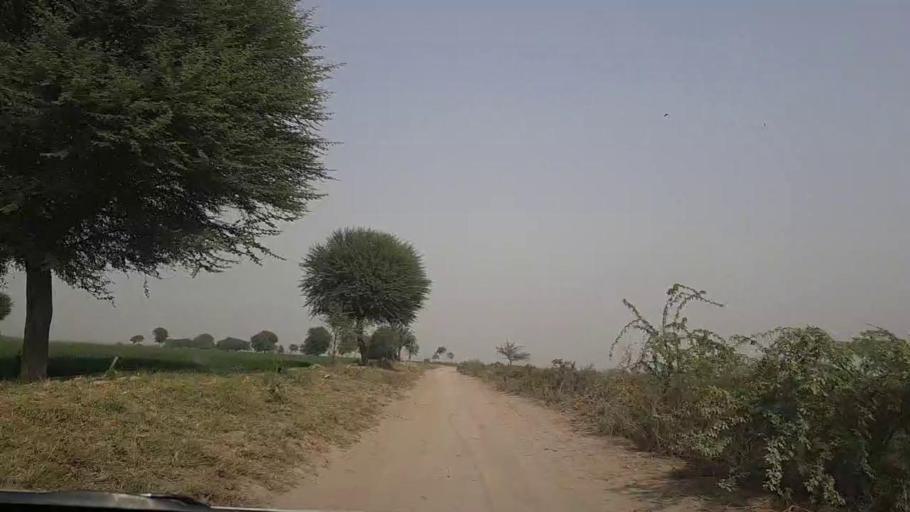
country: PK
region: Sindh
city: Pithoro
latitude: 25.4600
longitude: 69.2531
